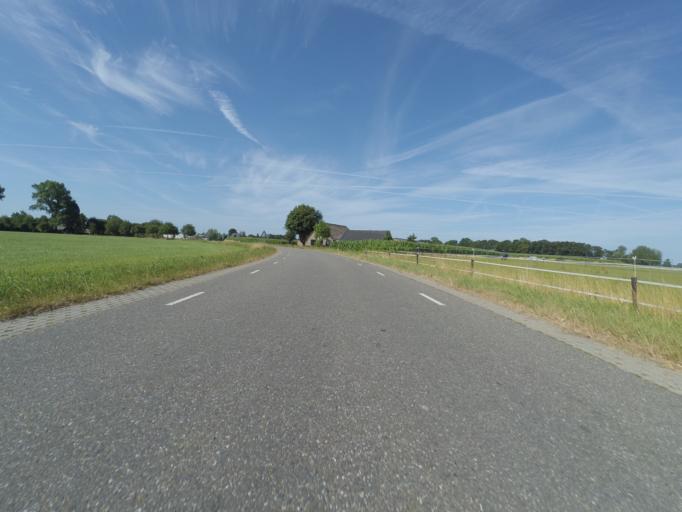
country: NL
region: Gelderland
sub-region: Gemeente Epe
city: Vaassen
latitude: 52.2585
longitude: 6.0304
